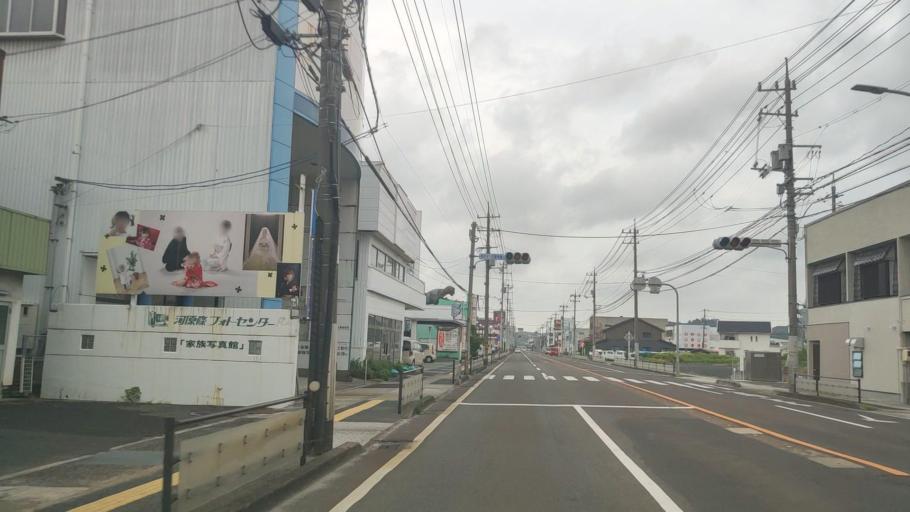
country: JP
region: Tottori
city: Kurayoshi
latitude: 35.4431
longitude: 133.8493
